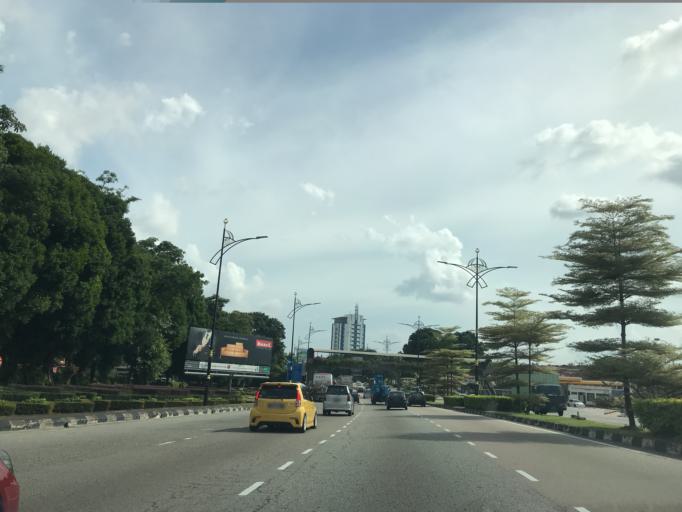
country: MY
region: Johor
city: Skudai
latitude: 1.5460
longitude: 103.6573
